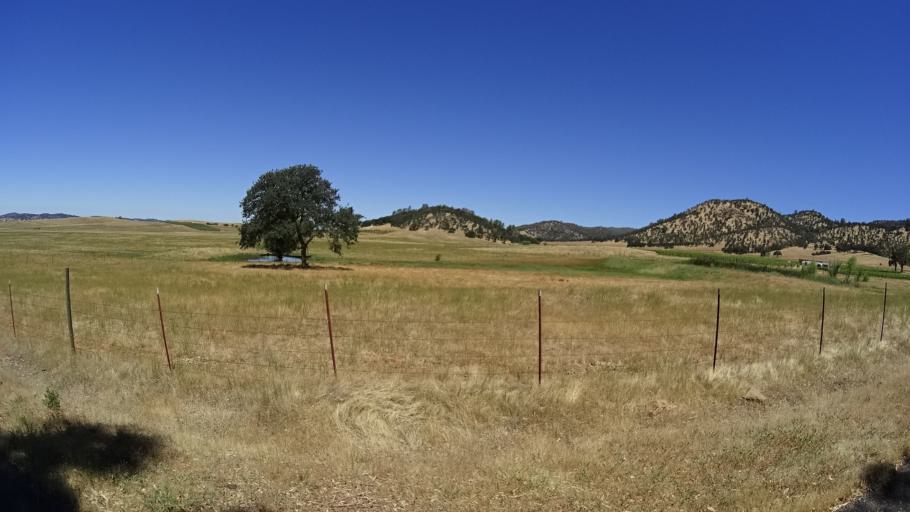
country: US
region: California
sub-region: Calaveras County
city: Copperopolis
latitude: 38.0432
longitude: -120.6954
